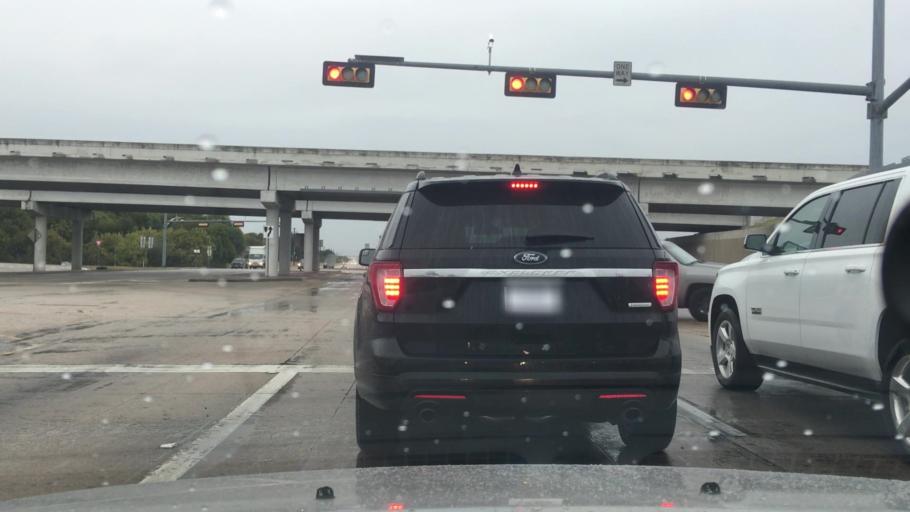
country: US
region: Texas
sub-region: Denton County
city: Denton
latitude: 33.2330
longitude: -97.0906
